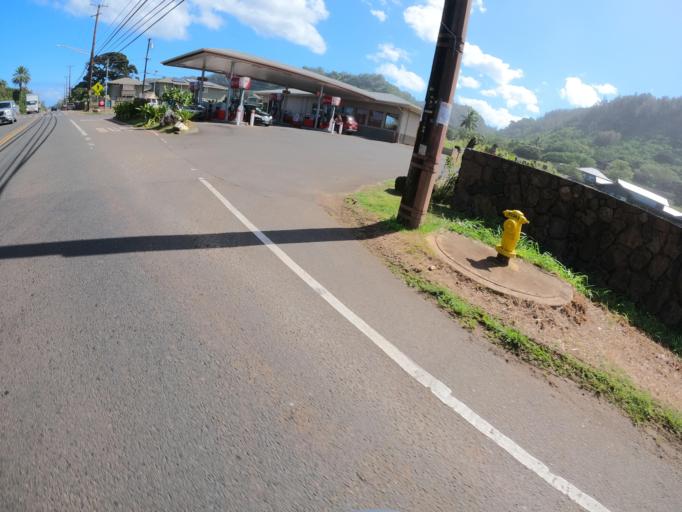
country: US
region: Hawaii
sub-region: Honolulu County
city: Pupukea
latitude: 21.6711
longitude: -158.0433
